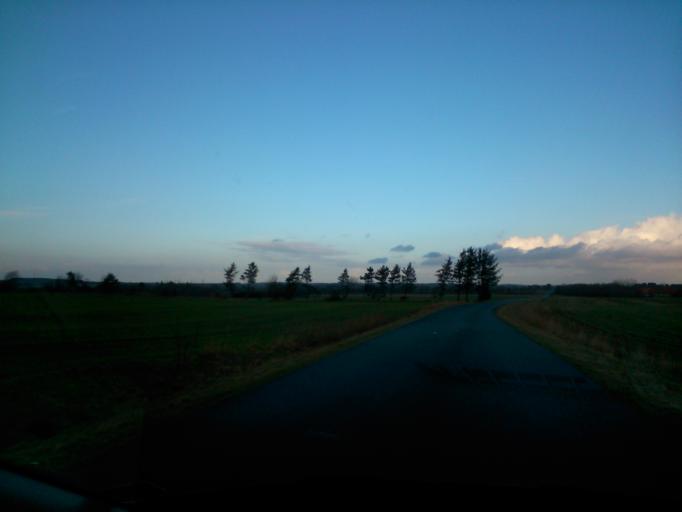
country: DK
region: Central Jutland
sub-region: Ringkobing-Skjern Kommune
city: Videbaek
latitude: 56.0434
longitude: 8.5683
